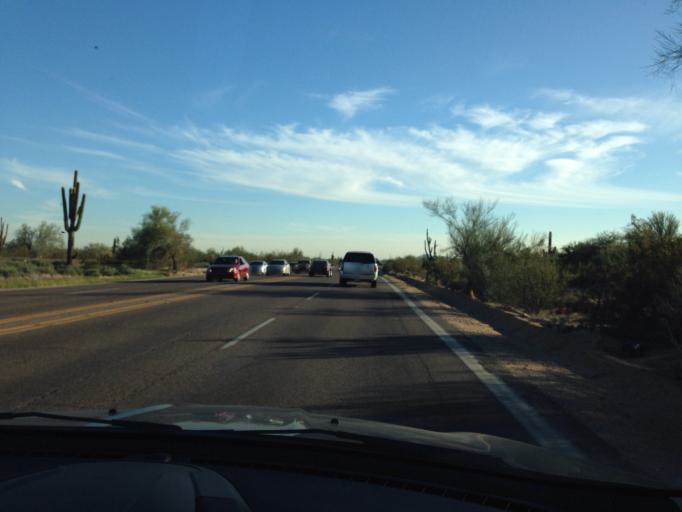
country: US
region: Arizona
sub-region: Maricopa County
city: Cave Creek
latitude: 33.7318
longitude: -111.9780
